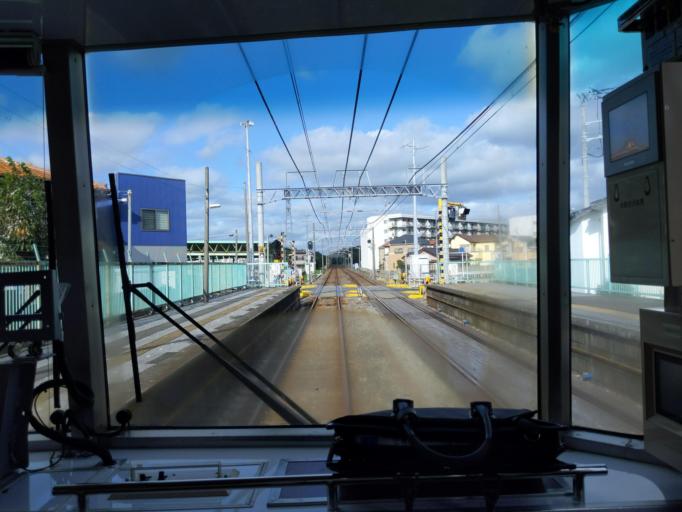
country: JP
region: Chiba
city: Funabashi
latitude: 35.7386
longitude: 140.0268
